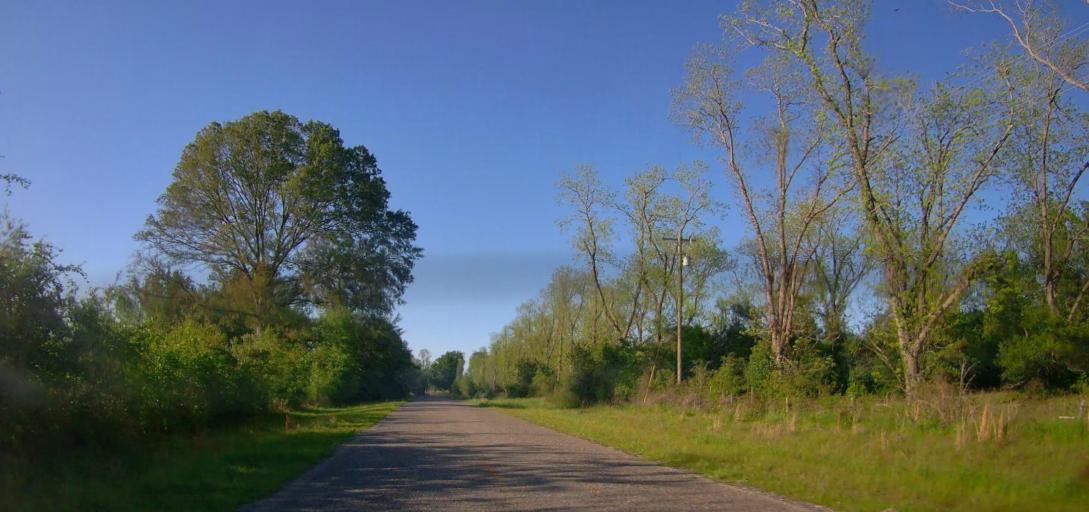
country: US
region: Georgia
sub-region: Ben Hill County
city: Fitzgerald
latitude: 31.6919
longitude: -83.1536
